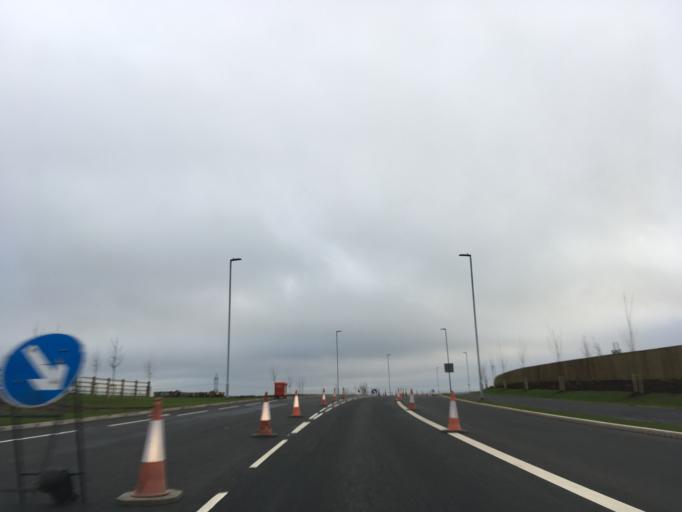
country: GB
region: England
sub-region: South Gloucestershire
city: Stoke Gifford
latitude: 51.5164
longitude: -2.5293
